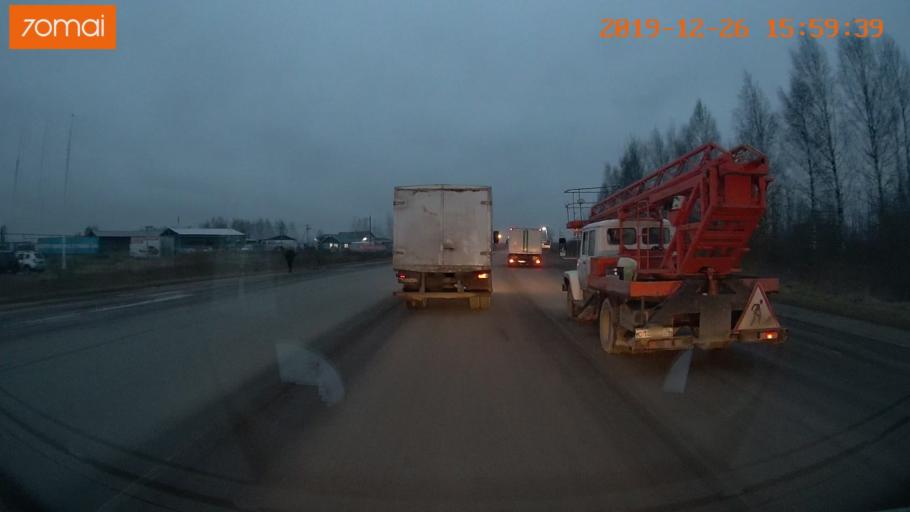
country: RU
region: Jaroslavl
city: Rybinsk
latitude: 58.0302
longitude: 38.8047
